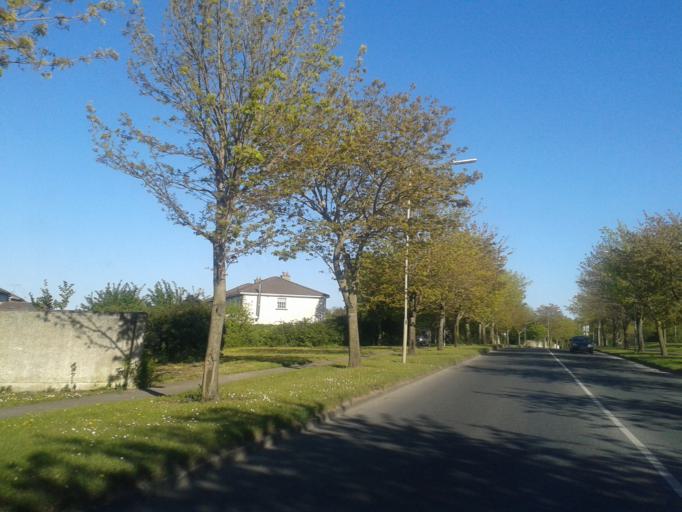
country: IE
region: Leinster
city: Kinsealy-Drinan
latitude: 53.4460
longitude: -6.1999
